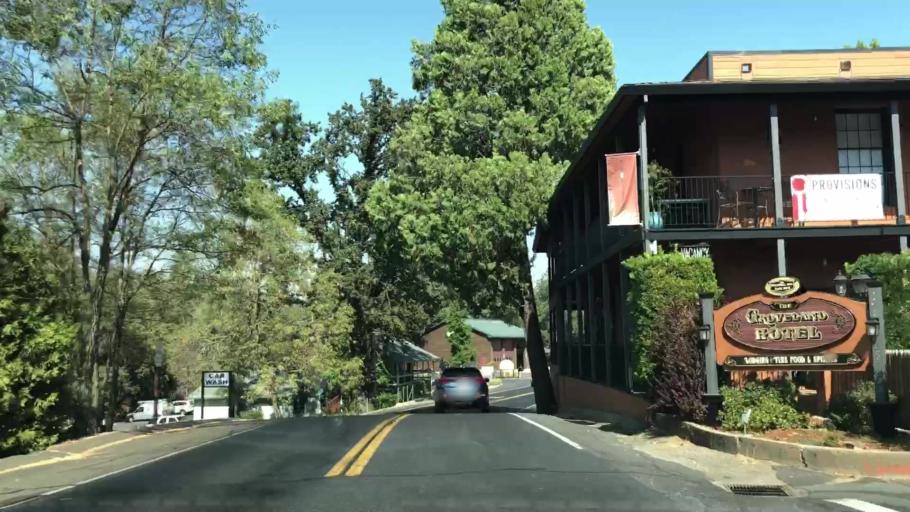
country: US
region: California
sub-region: Tuolumne County
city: Tuolumne City
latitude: 37.8393
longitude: -120.2298
